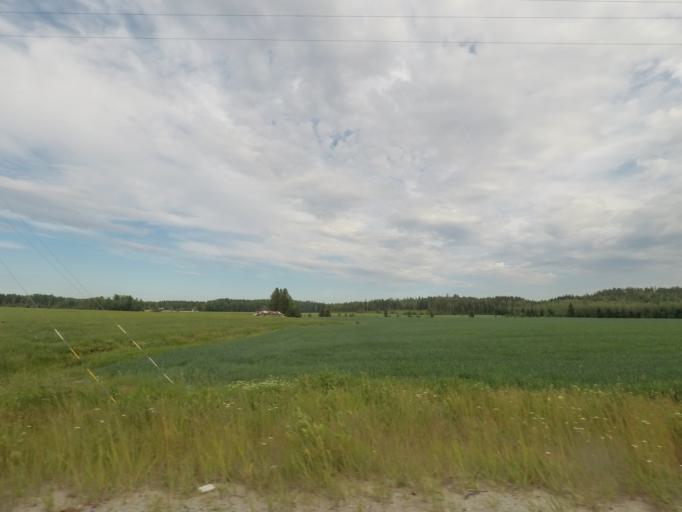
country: FI
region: Paijanne Tavastia
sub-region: Lahti
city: Lahti
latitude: 60.9240
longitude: 25.5770
